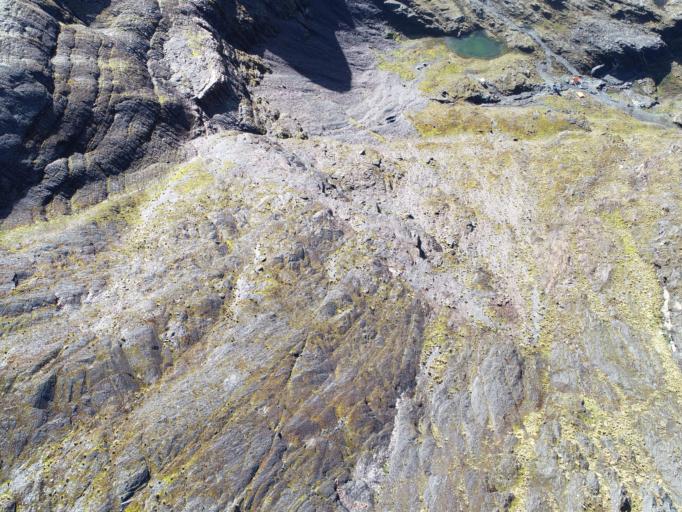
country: PE
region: Puno
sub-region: San Antonio De Putina
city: Sina
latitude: -14.7382
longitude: -69.0548
